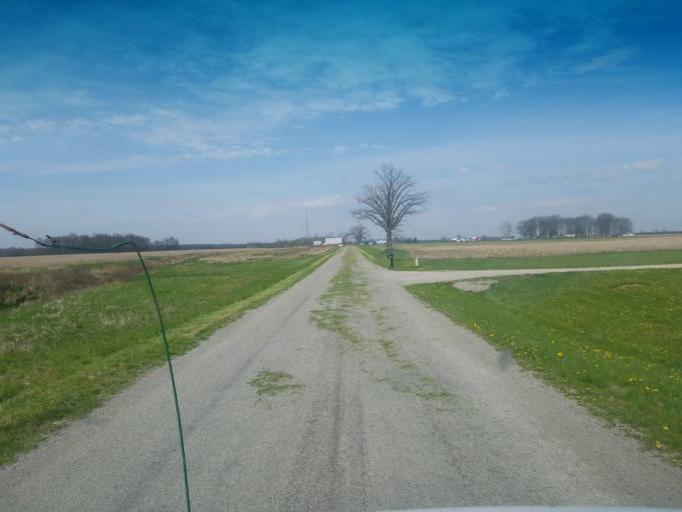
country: US
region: Ohio
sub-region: Union County
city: Richwood
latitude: 40.4829
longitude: -83.4627
